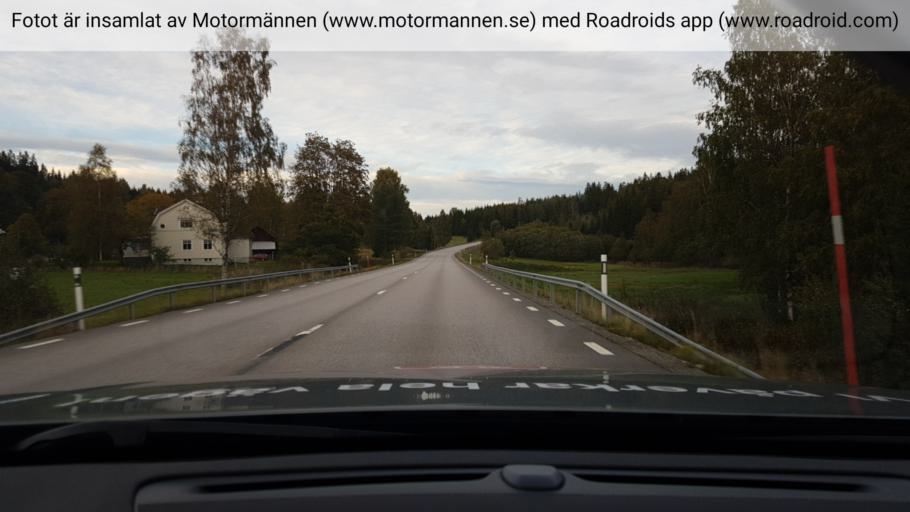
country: SE
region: Vaestra Goetaland
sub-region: Bengtsfors Kommun
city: Dals Langed
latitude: 59.0247
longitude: 12.3848
